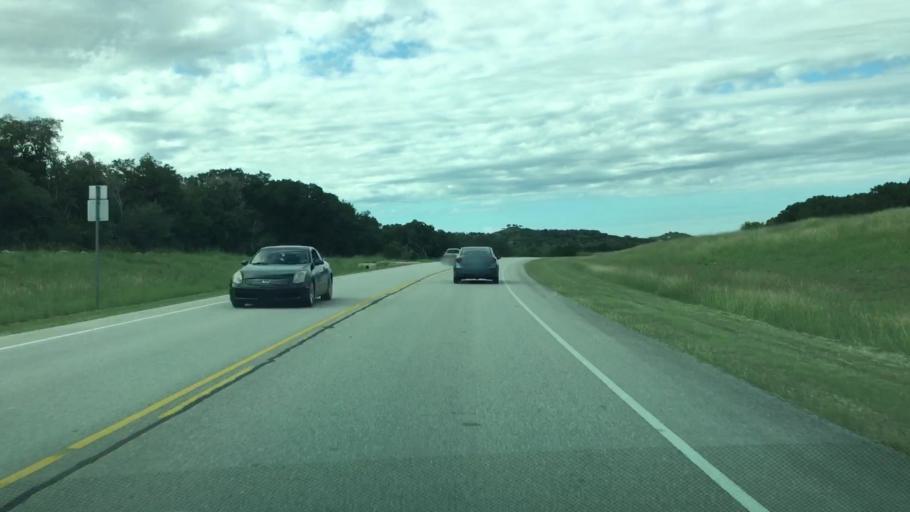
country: US
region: Texas
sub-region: Hays County
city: Wimberley
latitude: 30.0085
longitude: -98.0826
